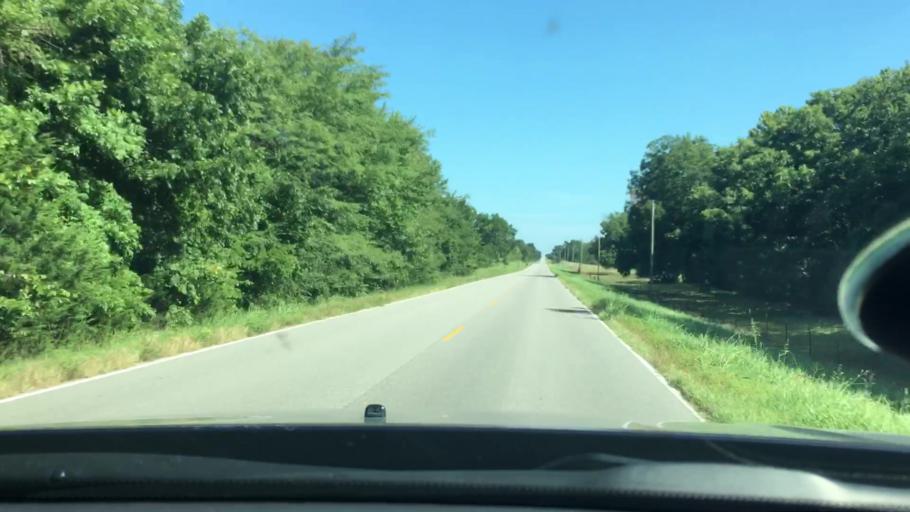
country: US
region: Oklahoma
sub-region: Johnston County
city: Tishomingo
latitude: 34.2826
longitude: -96.5487
